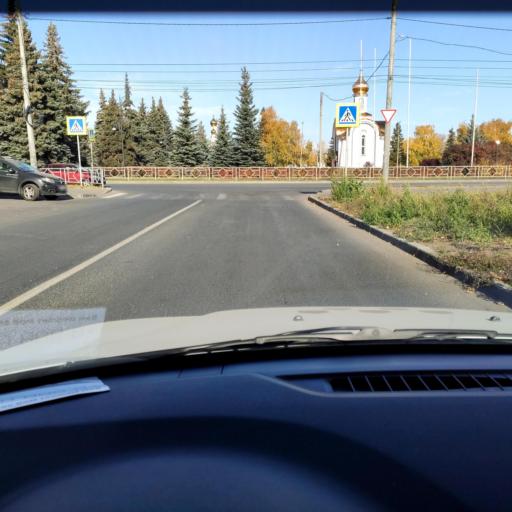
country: RU
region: Samara
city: Tol'yatti
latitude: 53.5060
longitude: 49.4198
